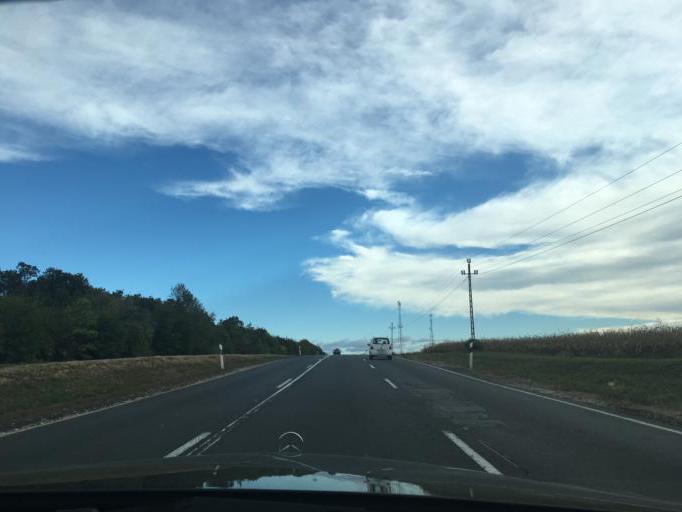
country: HU
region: Borsod-Abauj-Zemplen
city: Arnot
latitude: 48.1485
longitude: 20.8928
